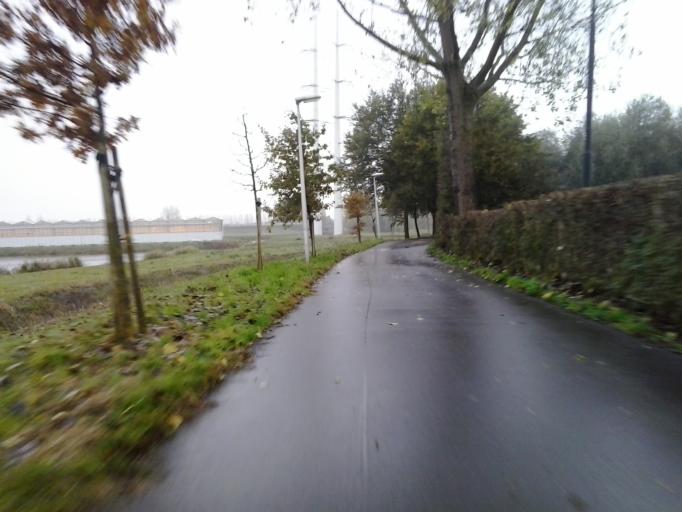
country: NL
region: South Holland
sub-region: Gemeente Zoetermeer
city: Zoetermeer
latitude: 52.0332
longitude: 4.5072
